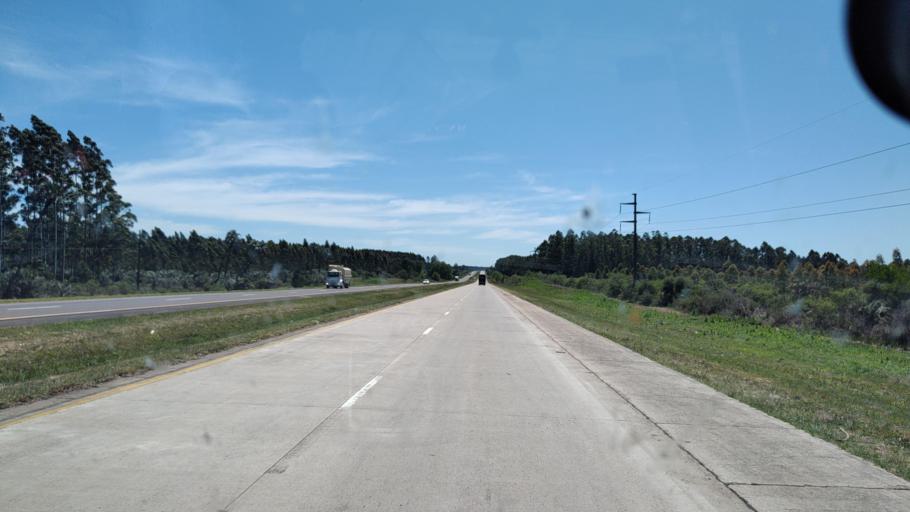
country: AR
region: Entre Rios
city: Ubajay
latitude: -31.8931
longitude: -58.3259
